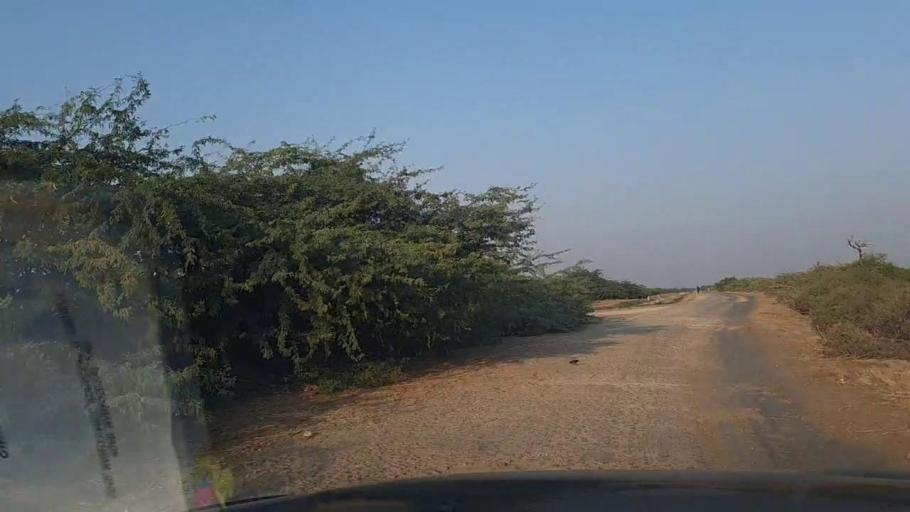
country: PK
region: Sindh
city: Keti Bandar
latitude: 24.2946
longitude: 67.5842
